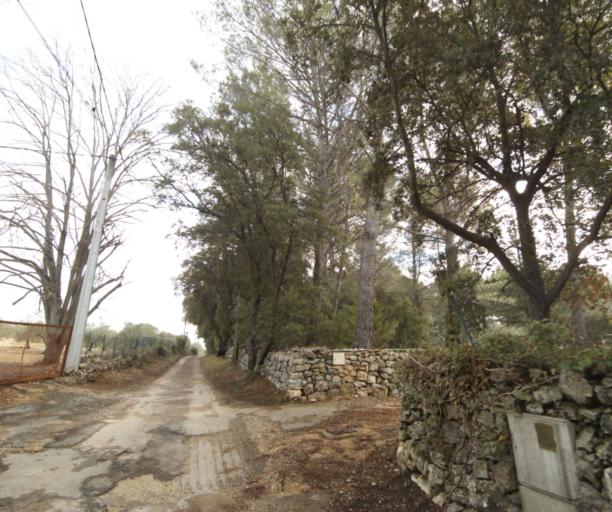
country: FR
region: Provence-Alpes-Cote d'Azur
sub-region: Departement du Var
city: Trans-en-Provence
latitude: 43.5021
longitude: 6.5023
